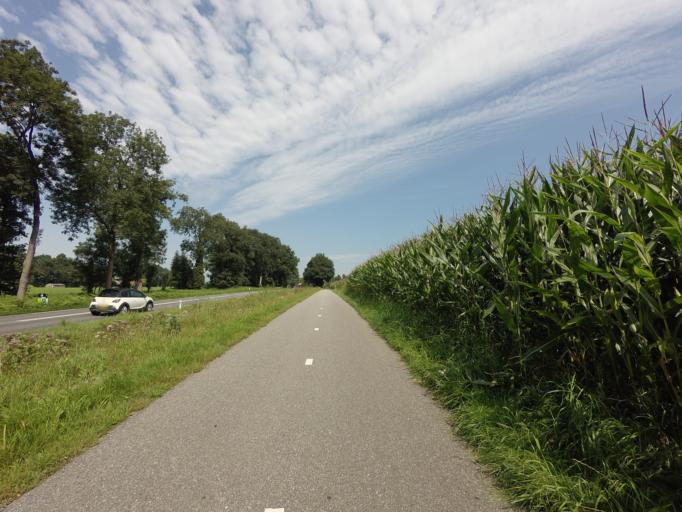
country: NL
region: Overijssel
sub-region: Gemeente Hof van Twente
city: Delden
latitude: 52.2343
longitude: 6.6905
